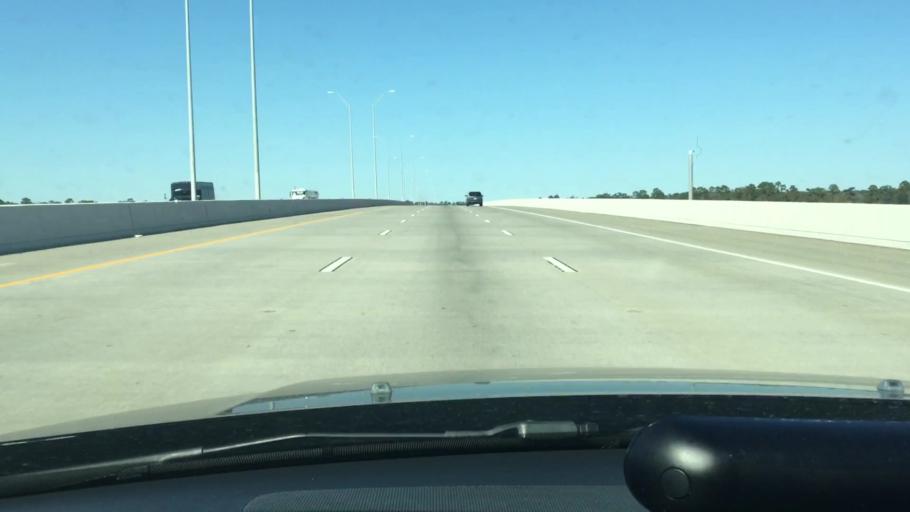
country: US
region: Texas
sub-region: Harris County
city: Cloverleaf
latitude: 29.8316
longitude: -95.1746
